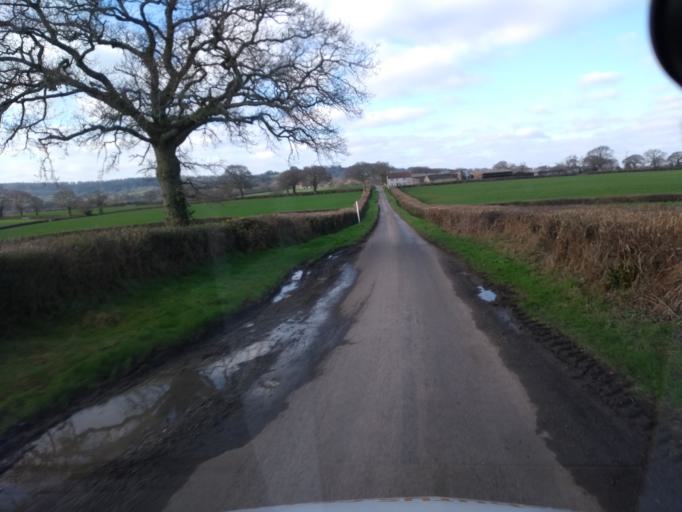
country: GB
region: England
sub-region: Somerset
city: Chard
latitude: 50.9335
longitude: -2.9924
